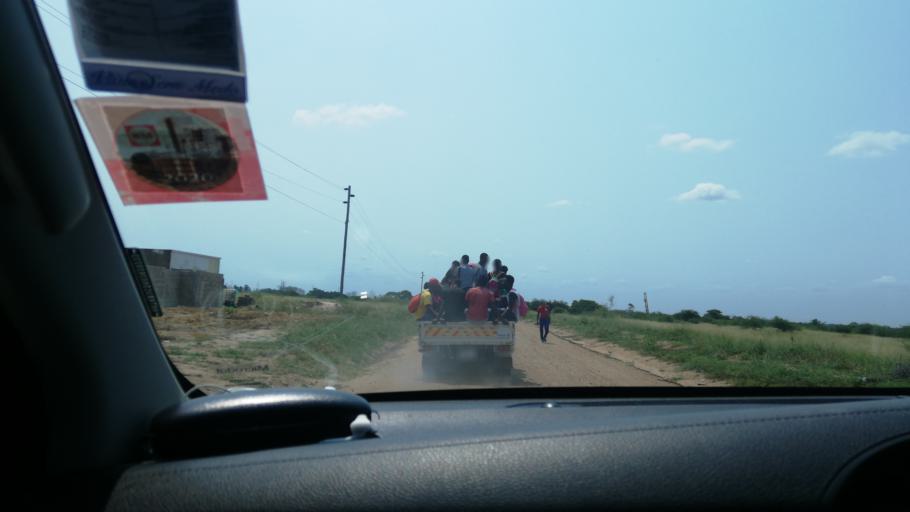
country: MZ
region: Maputo
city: Matola
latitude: -26.0628
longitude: 32.3901
